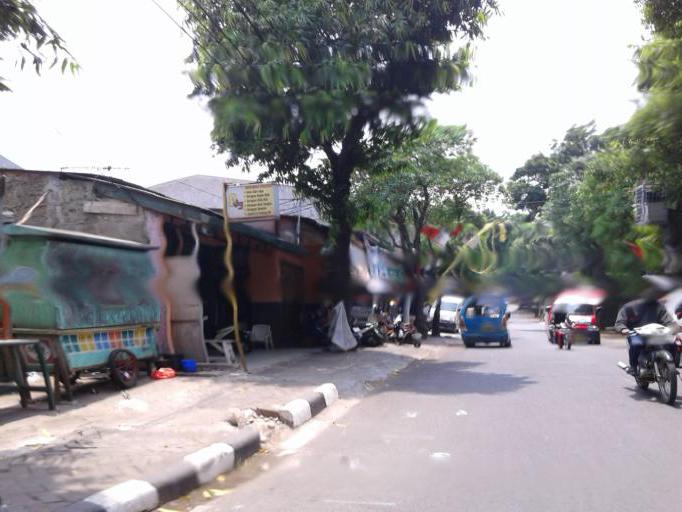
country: ID
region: West Java
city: Pamulang
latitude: -6.3132
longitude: 106.8006
